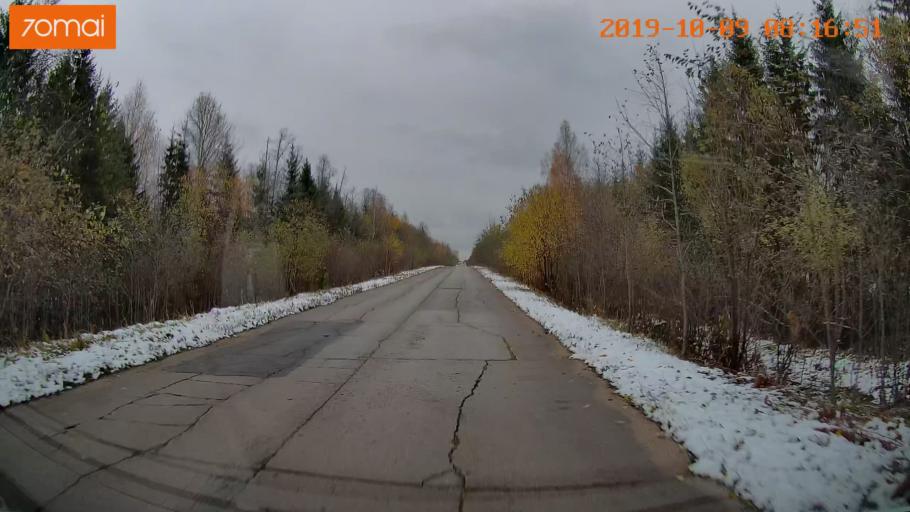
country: RU
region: Vologda
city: Gryazovets
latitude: 58.7377
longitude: 40.1952
